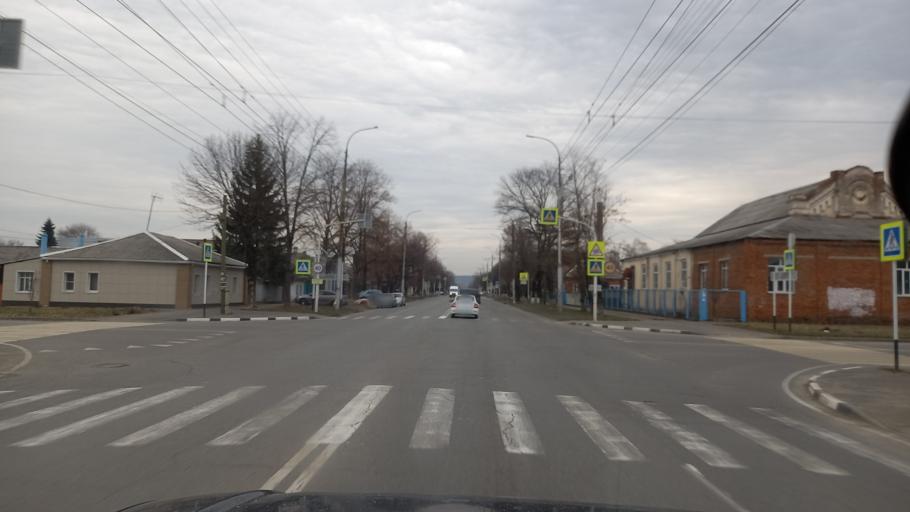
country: RU
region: Adygeya
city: Maykop
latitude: 44.6003
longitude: 40.1120
